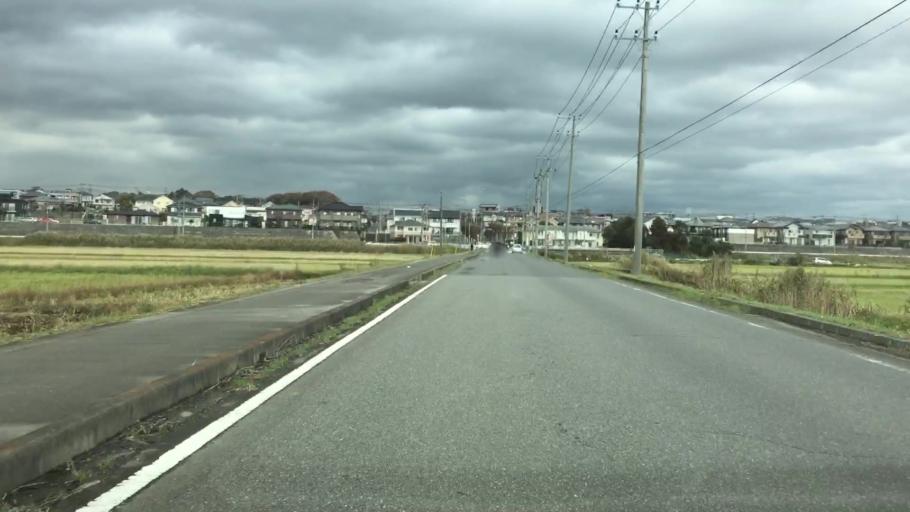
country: JP
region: Ibaraki
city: Toride
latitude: 35.8563
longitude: 140.1026
